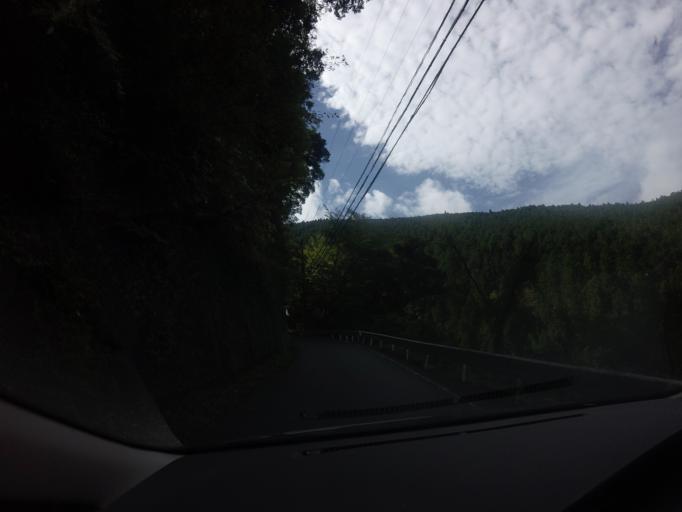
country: JP
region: Wakayama
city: Shingu
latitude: 33.9620
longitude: 135.8492
